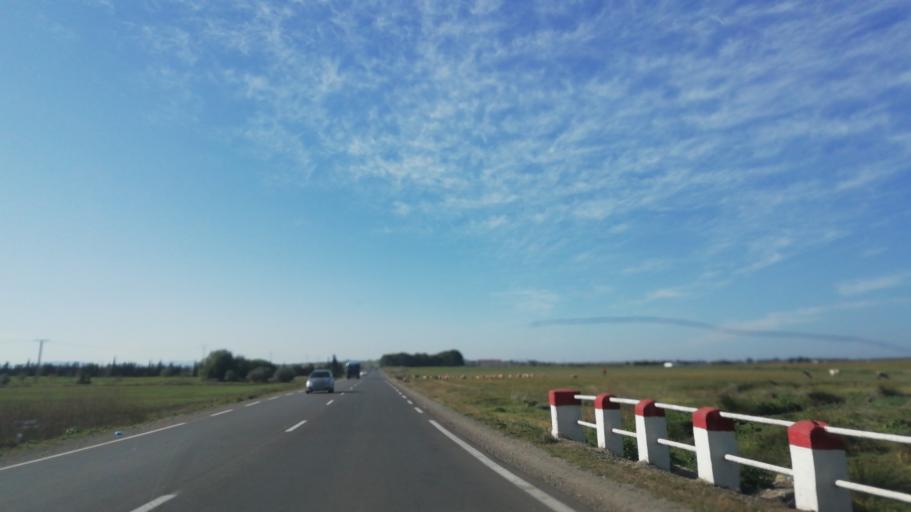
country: DZ
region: Tlemcen
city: Ouled Mimoun
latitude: 35.0342
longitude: -0.8609
